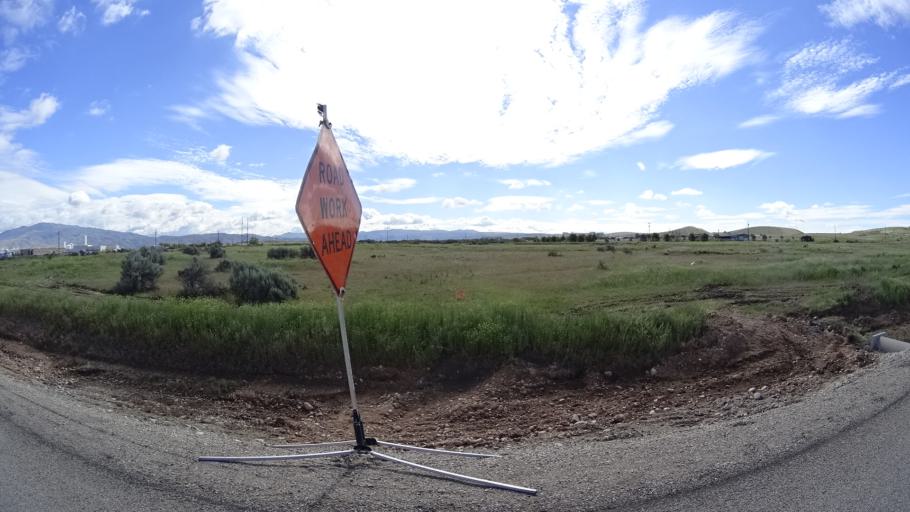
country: US
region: Idaho
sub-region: Ada County
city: Boise
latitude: 43.5149
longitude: -116.1514
